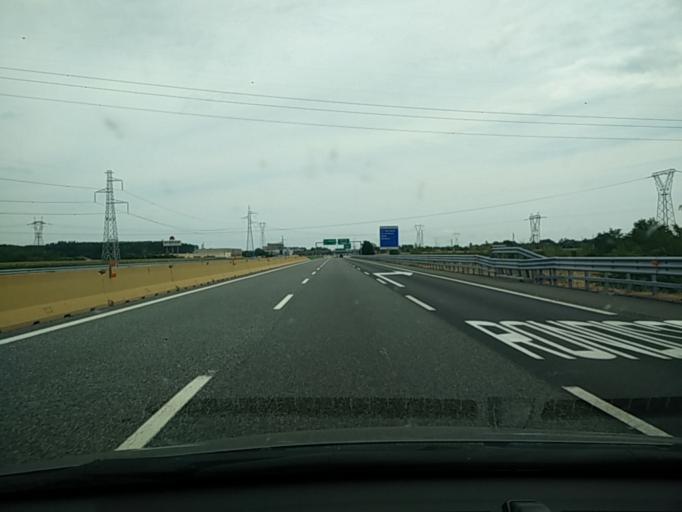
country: IT
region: Piedmont
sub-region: Provincia di Torino
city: Rondissone
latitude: 45.2322
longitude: 7.9446
